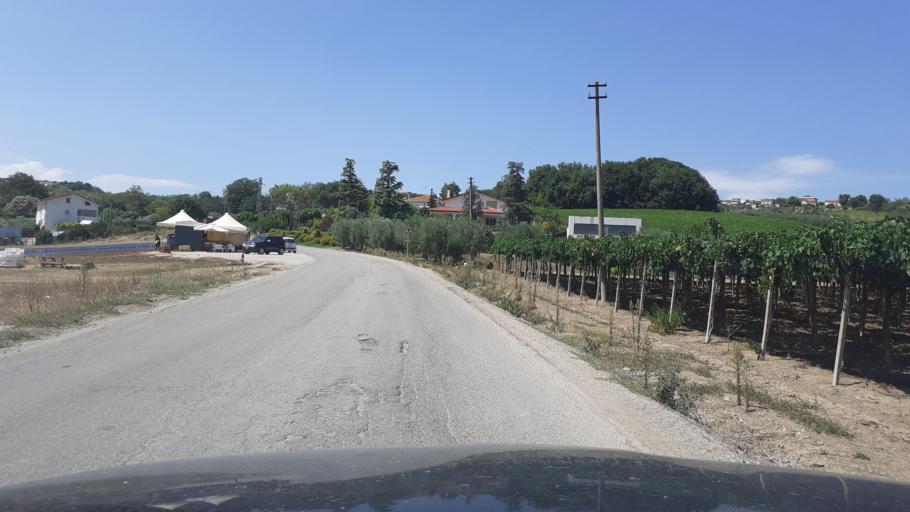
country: IT
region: Abruzzo
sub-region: Provincia di Chieti
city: Santa Maria Imbaro
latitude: 42.2154
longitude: 14.4651
